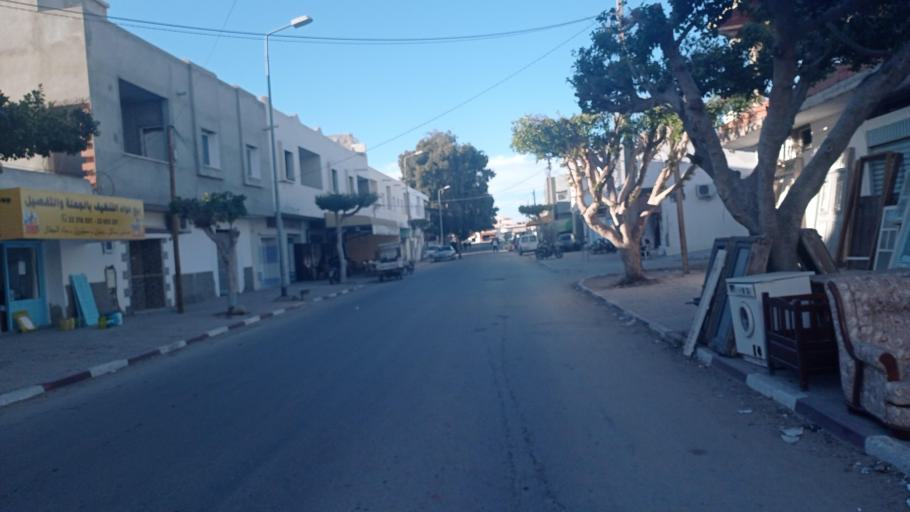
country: TN
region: Qabis
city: Gabes
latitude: 33.8409
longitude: 10.1172
